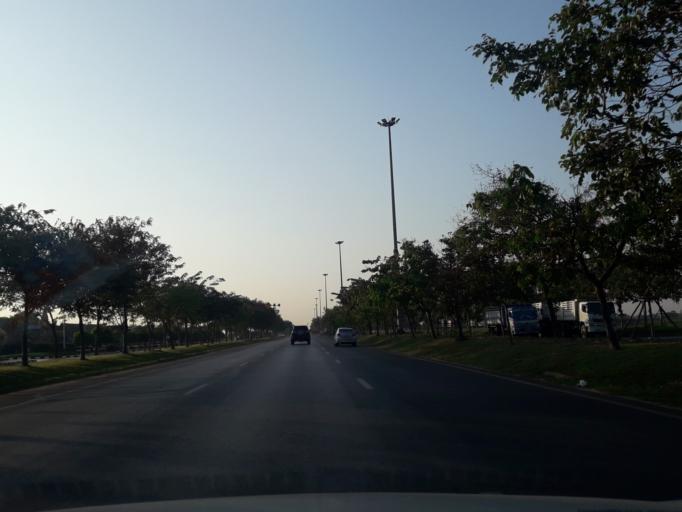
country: TH
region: Phra Nakhon Si Ayutthaya
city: Bang Pa-in
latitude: 14.2147
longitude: 100.5443
